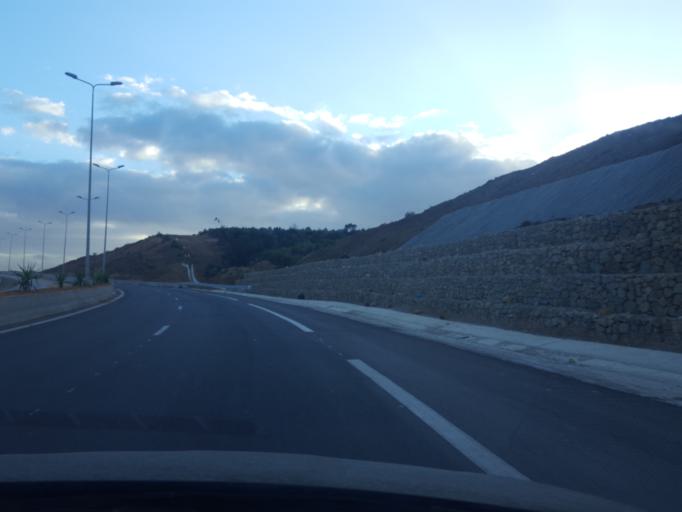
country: TN
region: Tunis
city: Hammam-Lif
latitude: 36.6599
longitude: 10.3732
